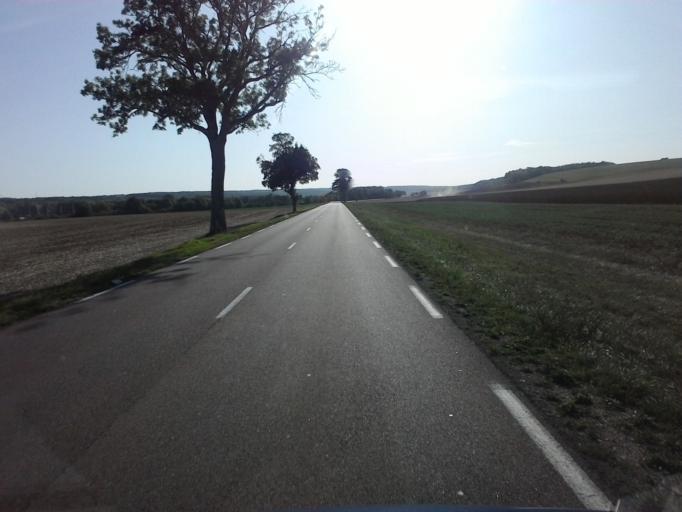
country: FR
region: Champagne-Ardenne
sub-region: Departement de l'Aube
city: Bar-sur-Seine
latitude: 48.1350
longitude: 4.3265
